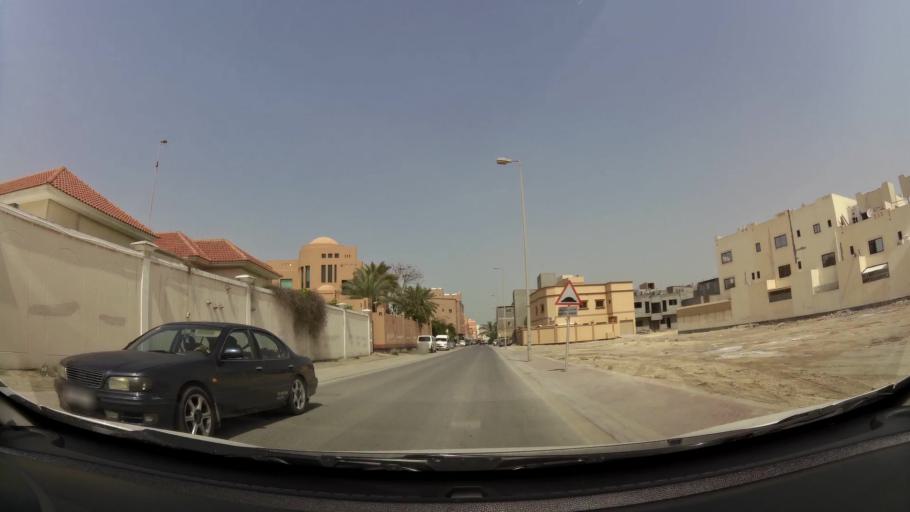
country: BH
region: Manama
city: Jidd Hafs
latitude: 26.2254
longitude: 50.4808
